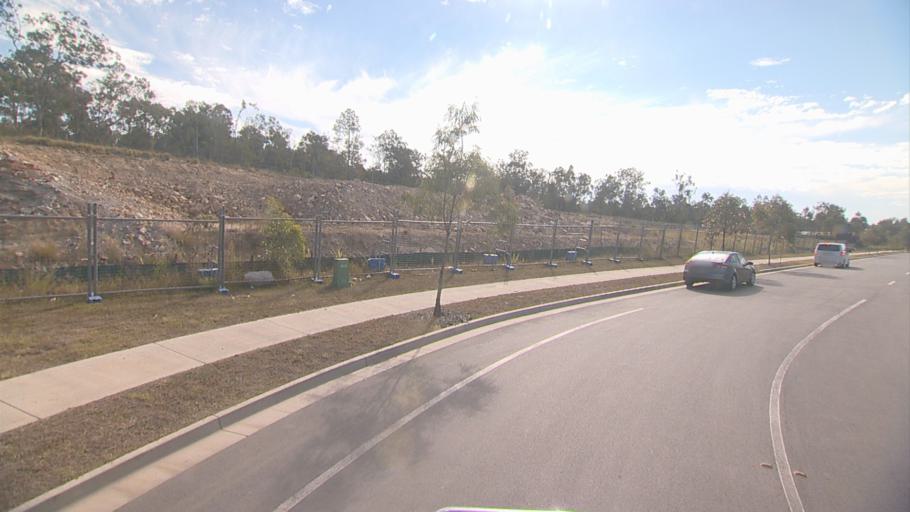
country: AU
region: Queensland
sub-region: Logan
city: Chambers Flat
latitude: -27.8035
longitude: 153.0998
